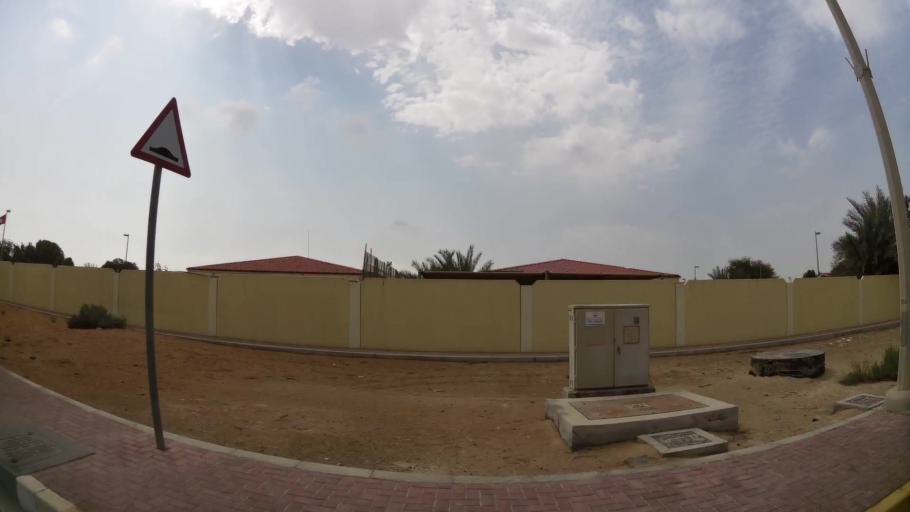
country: AE
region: Abu Dhabi
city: Abu Dhabi
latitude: 24.5213
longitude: 54.6796
